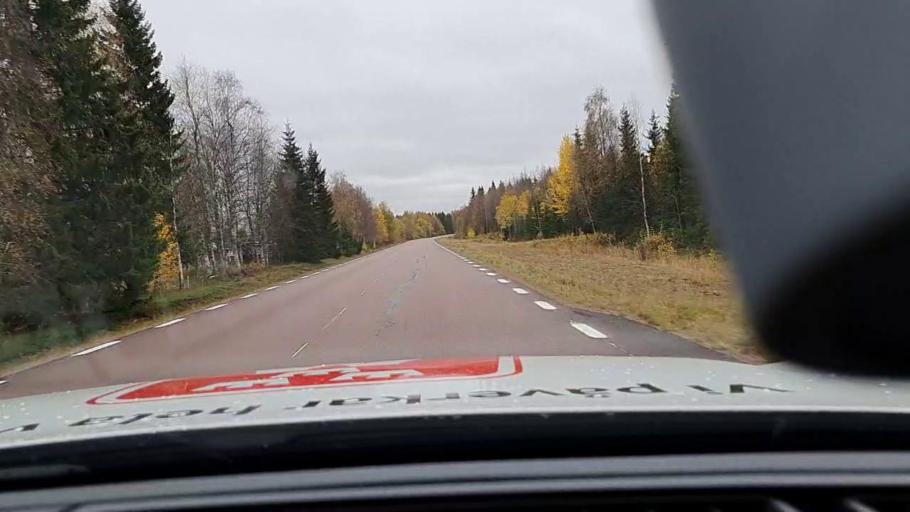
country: FI
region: Lapland
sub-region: Kemi-Tornio
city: Tornio
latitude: 66.0527
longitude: 23.9388
